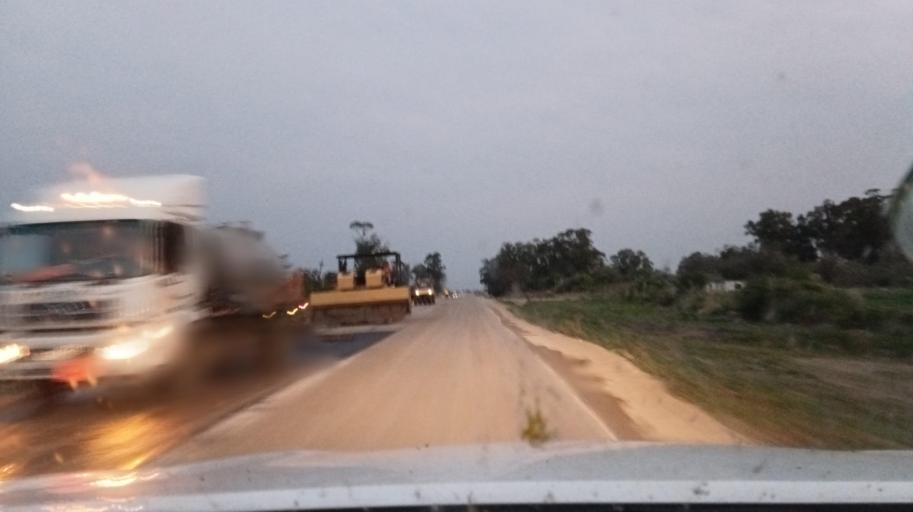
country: UY
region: Canelones
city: Santa Rosa
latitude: -34.5587
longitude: -56.1028
